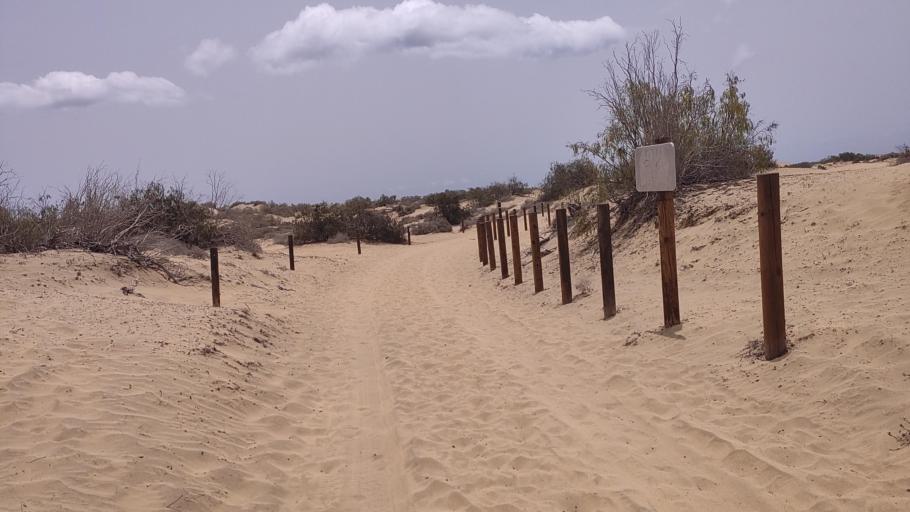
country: ES
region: Canary Islands
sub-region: Provincia de Las Palmas
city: Maspalomas
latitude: 27.7445
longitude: -15.5912
